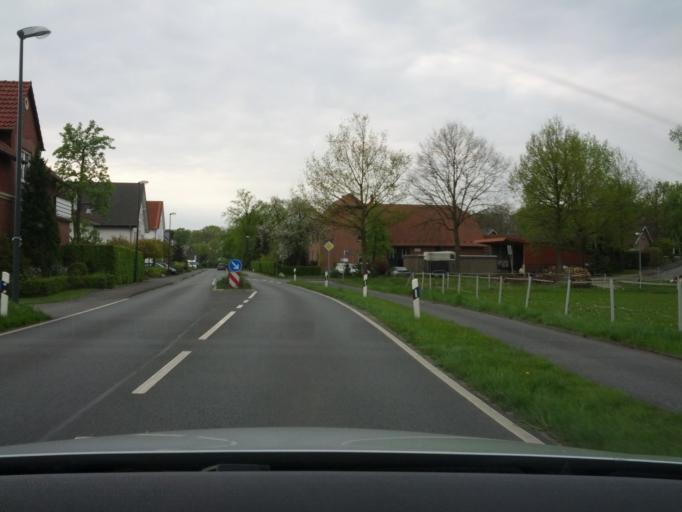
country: DE
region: North Rhine-Westphalia
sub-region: Regierungsbezirk Detmold
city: Guetersloh
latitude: 51.9409
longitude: 8.4160
